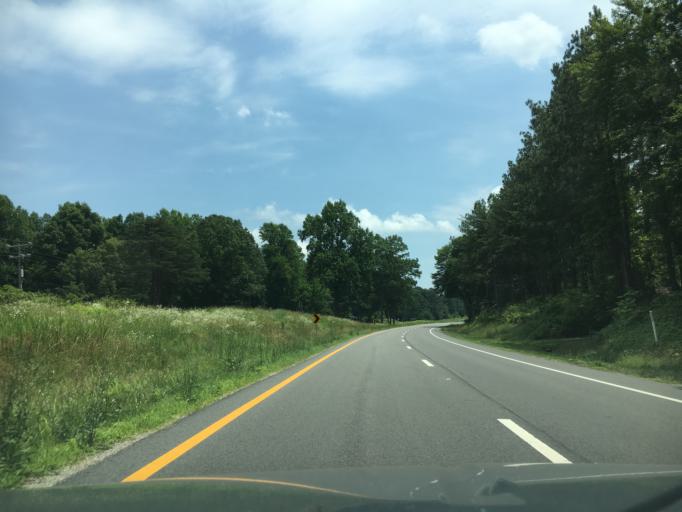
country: US
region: Virginia
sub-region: Buckingham County
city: Buckingham
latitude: 37.5464
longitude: -78.5215
